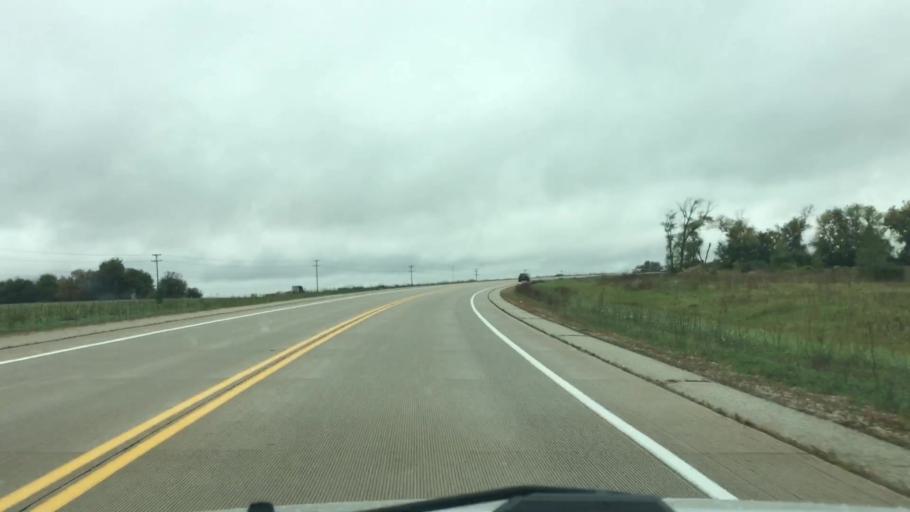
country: US
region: Wisconsin
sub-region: Walworth County
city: Whitewater
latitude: 42.8173
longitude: -88.7306
